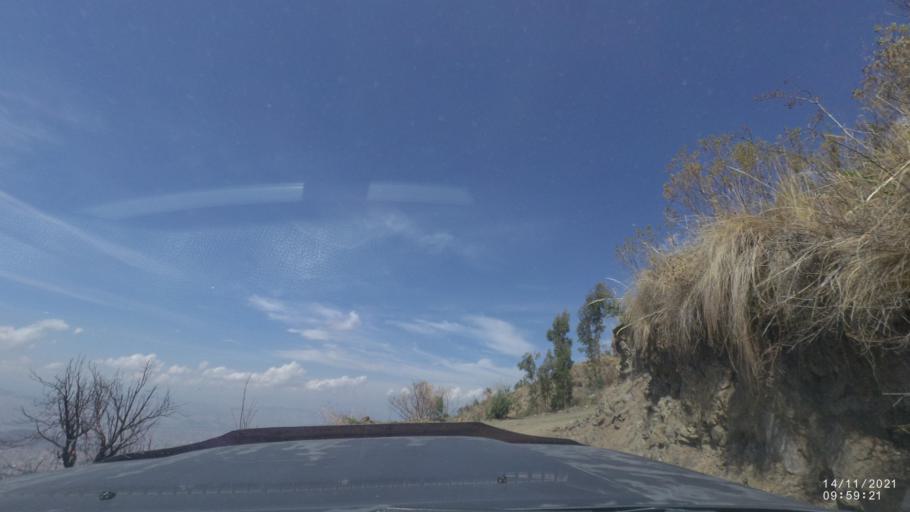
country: BO
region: Cochabamba
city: Cochabamba
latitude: -17.3541
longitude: -66.0883
